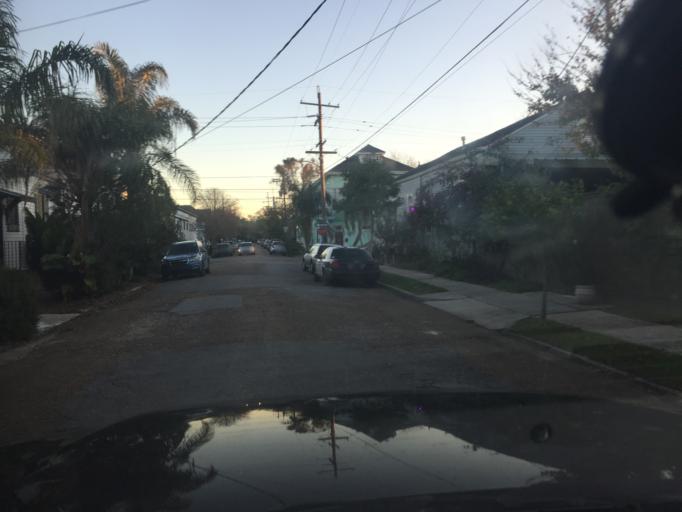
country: US
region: Louisiana
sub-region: Orleans Parish
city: New Orleans
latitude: 29.9755
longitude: -90.0874
